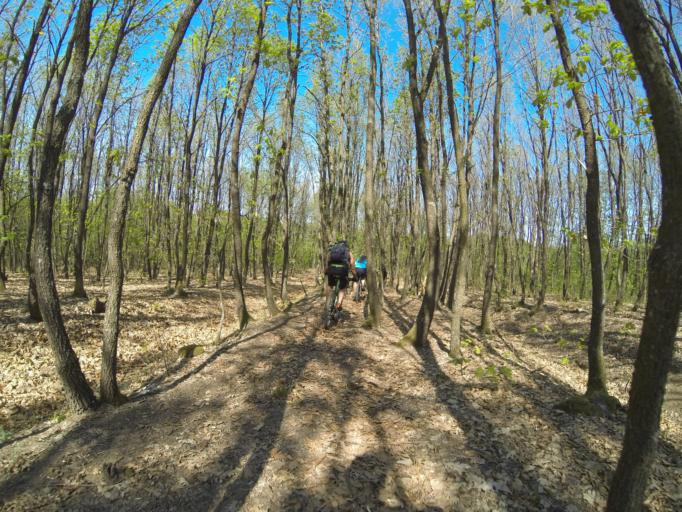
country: RO
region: Gorj
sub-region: Comuna Crusetu
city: Crusetu
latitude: 44.6125
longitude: 23.6498
